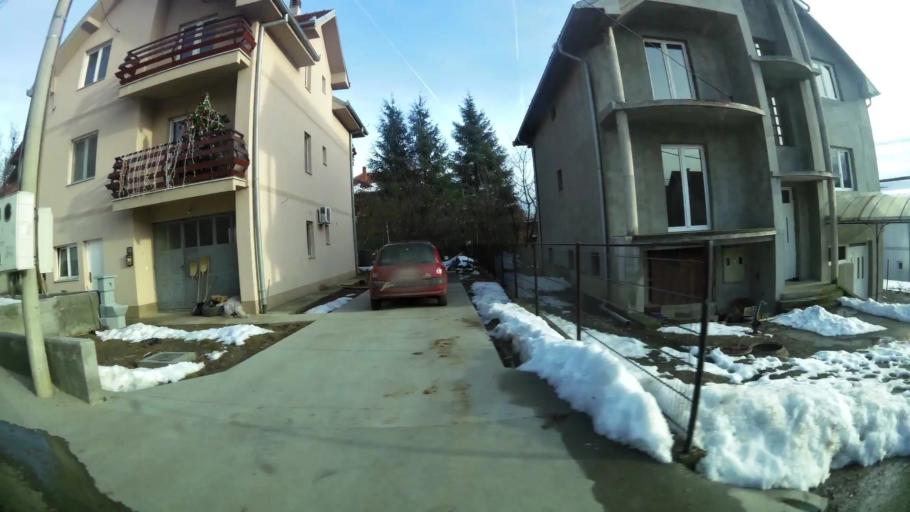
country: RS
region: Central Serbia
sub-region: Belgrade
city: Rakovica
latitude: 44.7385
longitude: 20.4546
